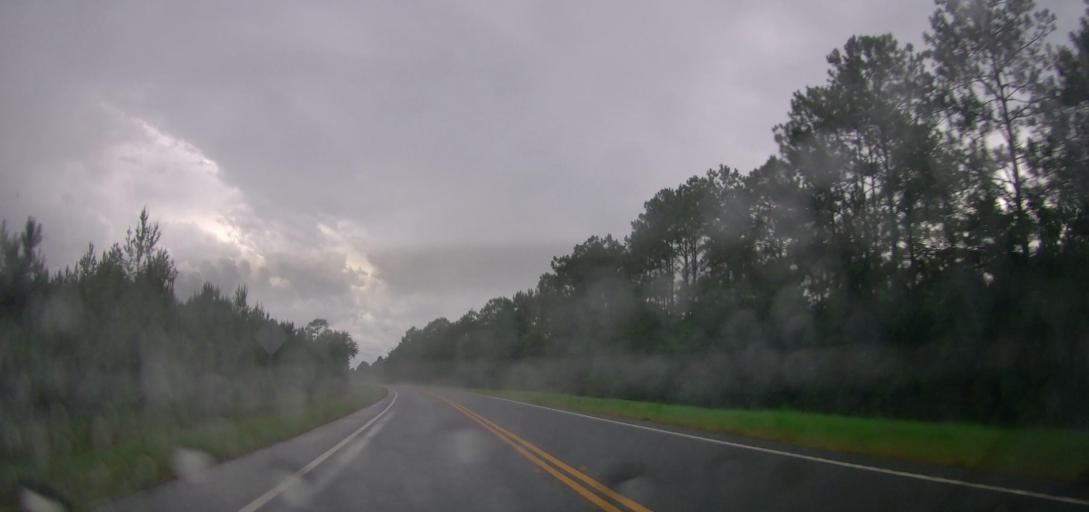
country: US
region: Georgia
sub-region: Brantley County
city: Nahunta
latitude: 31.3449
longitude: -81.7981
